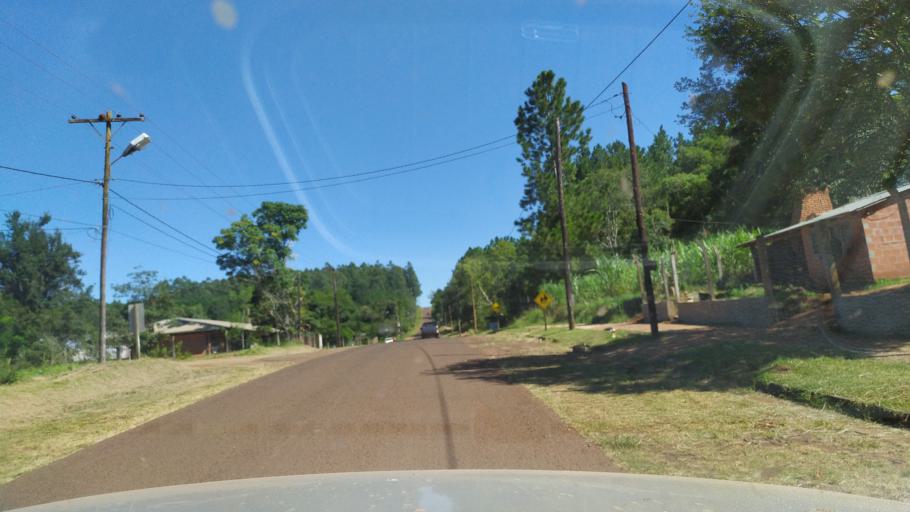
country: AR
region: Misiones
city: Caraguatay
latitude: -26.6521
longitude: -54.7435
